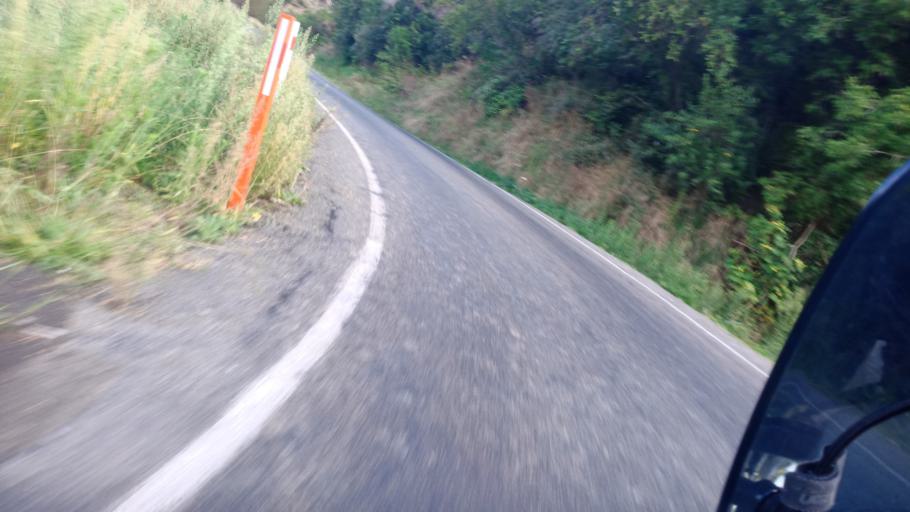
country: NZ
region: Gisborne
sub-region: Gisborne District
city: Gisborne
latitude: -38.5312
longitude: 177.5495
